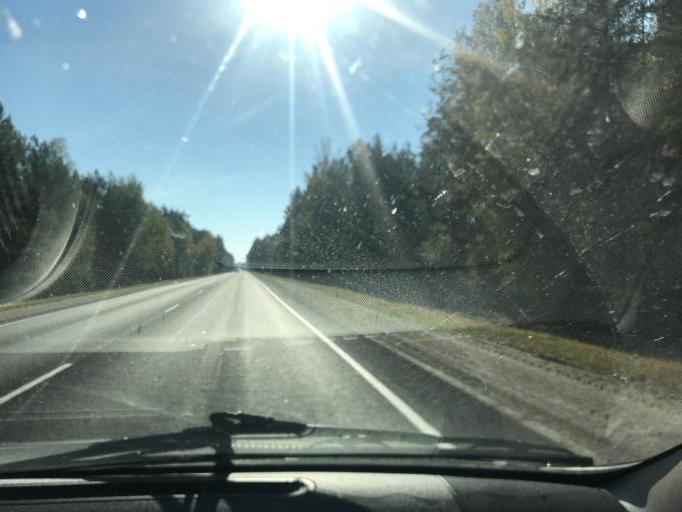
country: BY
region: Brest
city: Mikashevichy
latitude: 52.2640
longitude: 27.4408
